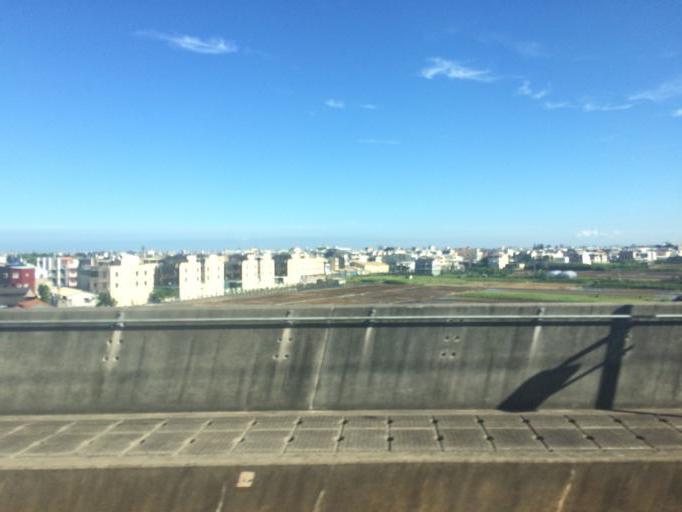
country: TW
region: Taiwan
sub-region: Nantou
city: Nantou
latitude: 23.8839
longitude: 120.5907
